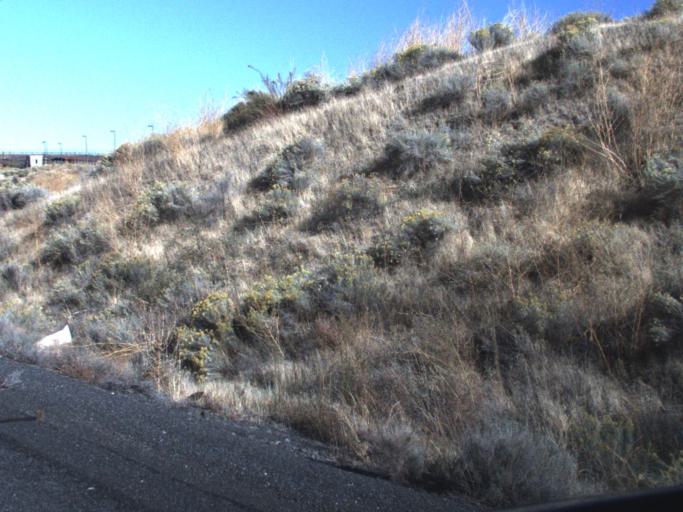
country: US
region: Washington
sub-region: Franklin County
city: Connell
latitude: 46.5632
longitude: -118.5456
